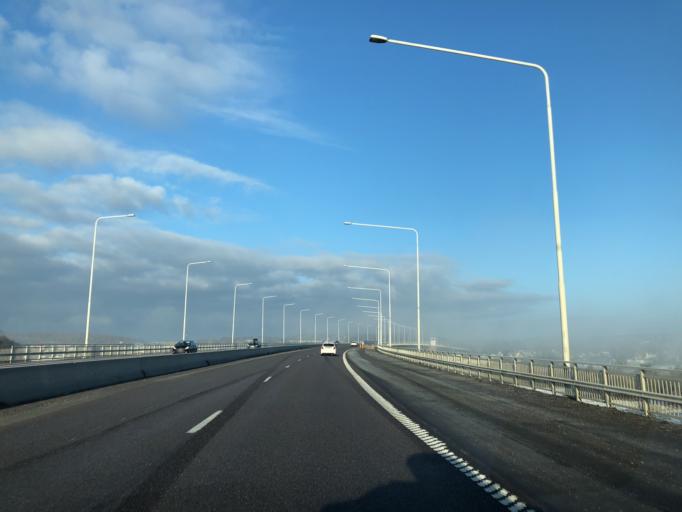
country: SE
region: Vaestra Goetaland
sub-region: Kungalvs Kommun
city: Kungalv
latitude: 57.8619
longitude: 11.9783
